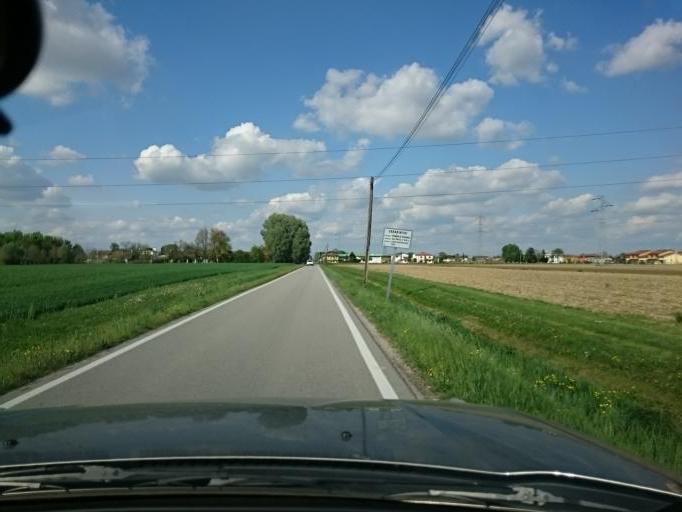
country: IT
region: Veneto
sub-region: Provincia di Padova
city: Villanova
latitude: 45.4780
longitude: 11.9825
